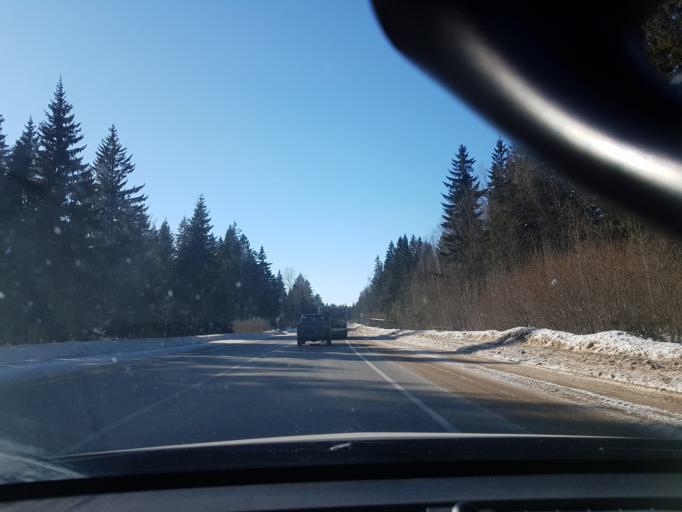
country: RU
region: Moskovskaya
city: Kostrovo
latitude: 55.9130
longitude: 36.7210
